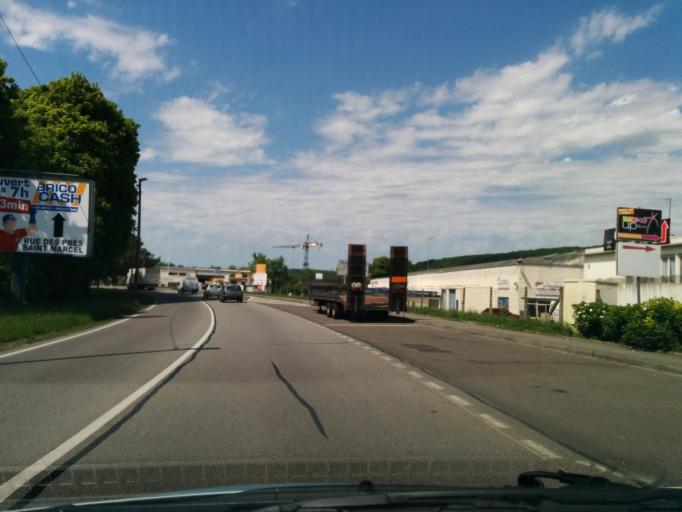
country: FR
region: Haute-Normandie
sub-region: Departement de l'Eure
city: Vernon
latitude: 49.0817
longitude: 1.5042
